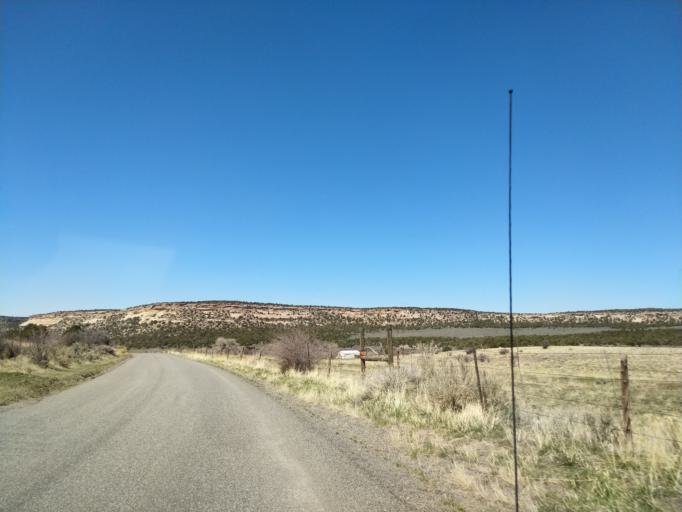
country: US
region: Colorado
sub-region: Mesa County
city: Loma
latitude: 38.9610
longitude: -109.0078
